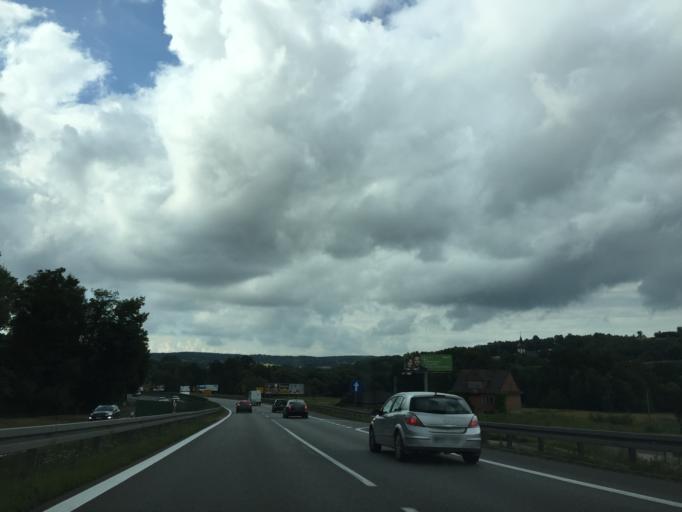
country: PL
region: Lesser Poland Voivodeship
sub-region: Powiat myslenicki
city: Glogoczow
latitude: 49.8893
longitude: 19.8785
